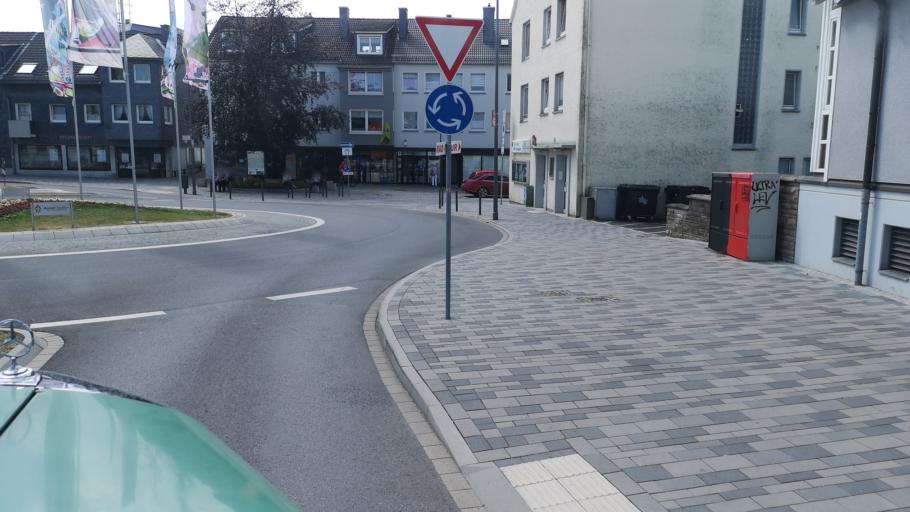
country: DE
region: North Rhine-Westphalia
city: Radevormwald
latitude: 51.2030
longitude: 7.3599
